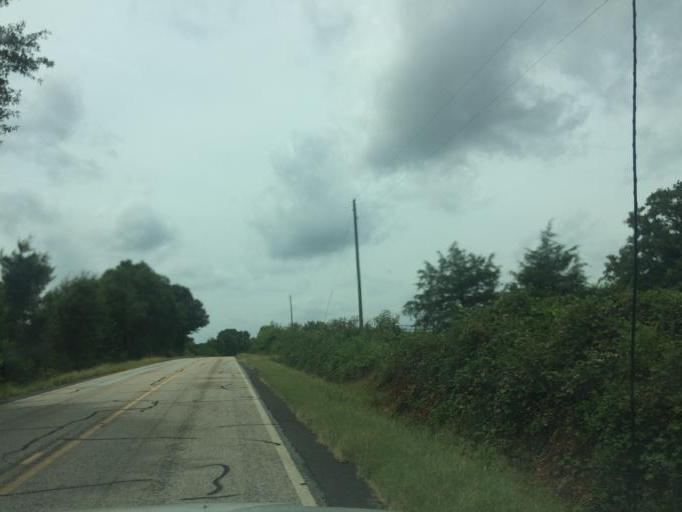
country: US
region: Georgia
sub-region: Hart County
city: Hartwell
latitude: 34.2681
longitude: -82.8829
